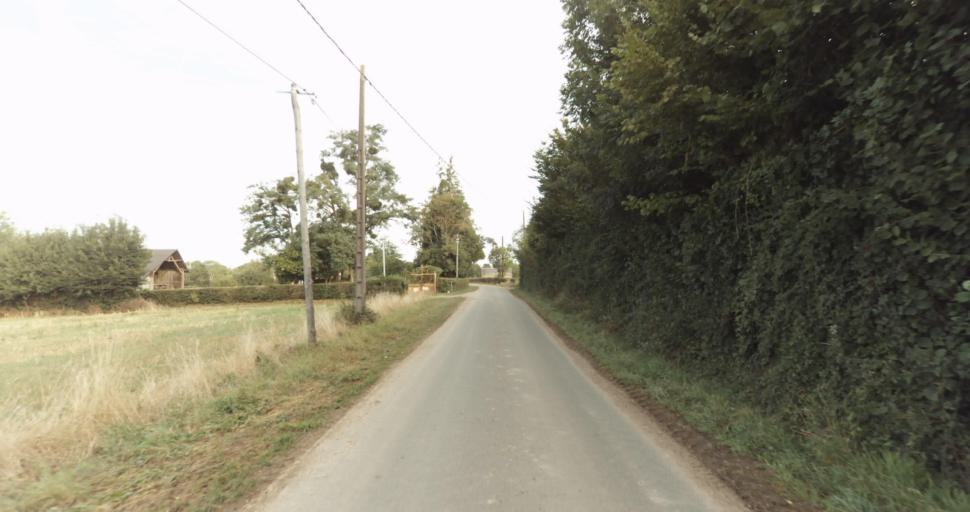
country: FR
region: Lower Normandy
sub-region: Departement de l'Orne
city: Vimoutiers
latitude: 48.8920
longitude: 0.2340
